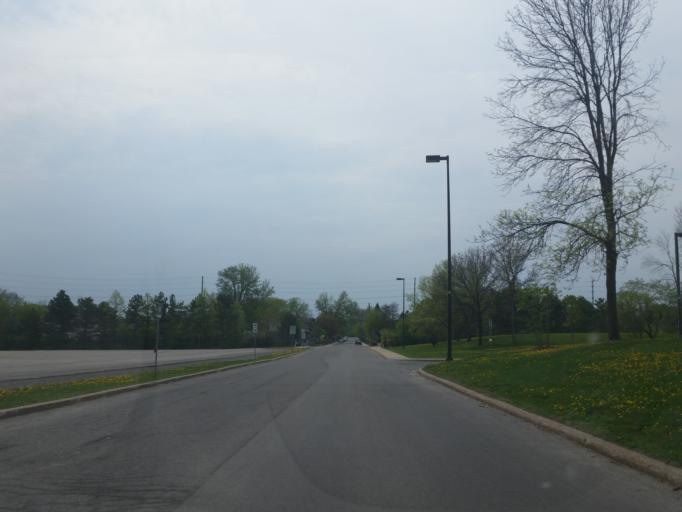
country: CA
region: Ontario
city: Ottawa
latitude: 45.4032
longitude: -75.7401
